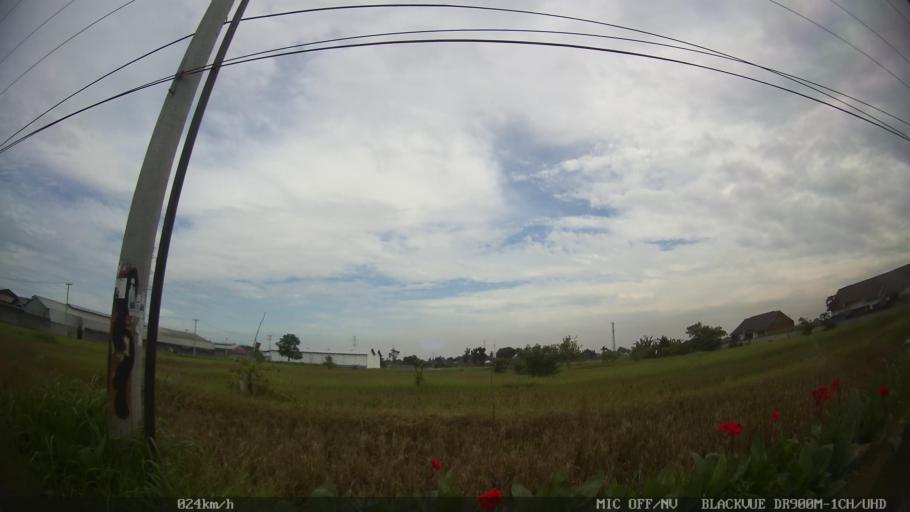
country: ID
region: North Sumatra
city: Sunggal
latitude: 3.6144
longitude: 98.5899
